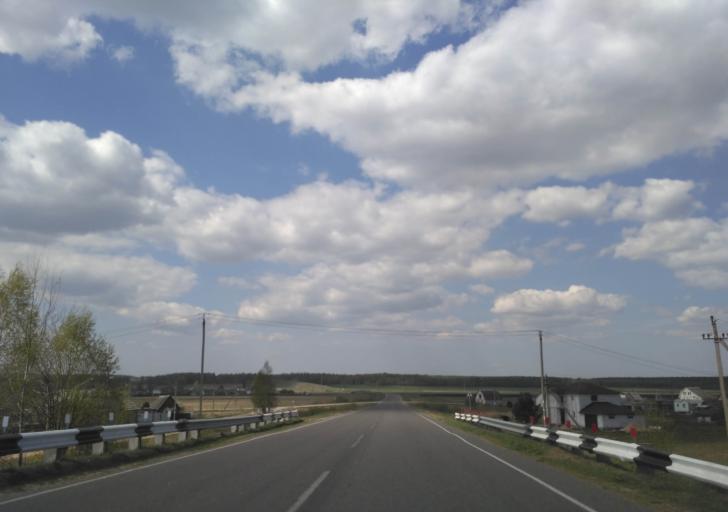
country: BY
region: Minsk
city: Vilyeyka
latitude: 54.5179
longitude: 26.9787
